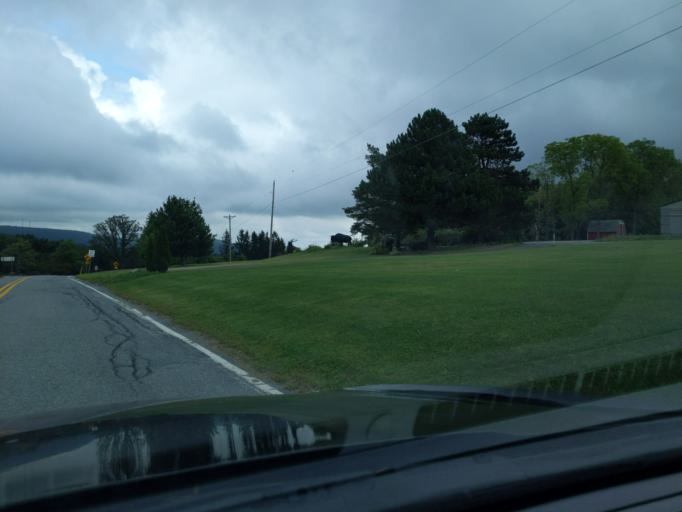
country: US
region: Pennsylvania
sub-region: Cambria County
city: Cresson
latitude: 40.3555
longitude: -78.5532
